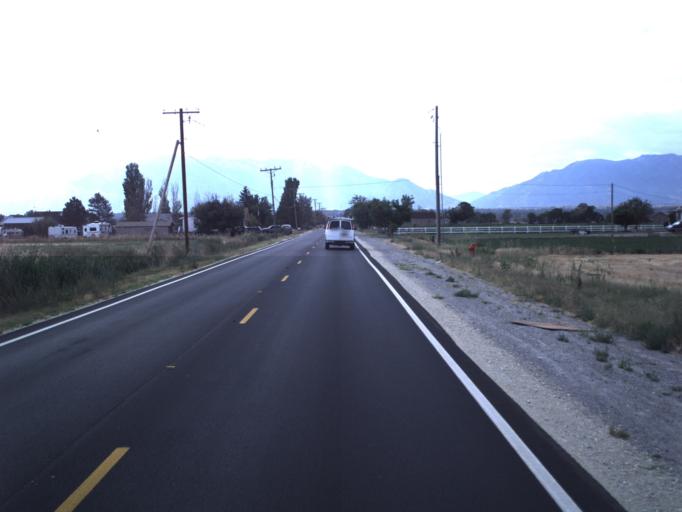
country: US
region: Utah
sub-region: Weber County
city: Hooper
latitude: 41.1639
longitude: -112.1100
